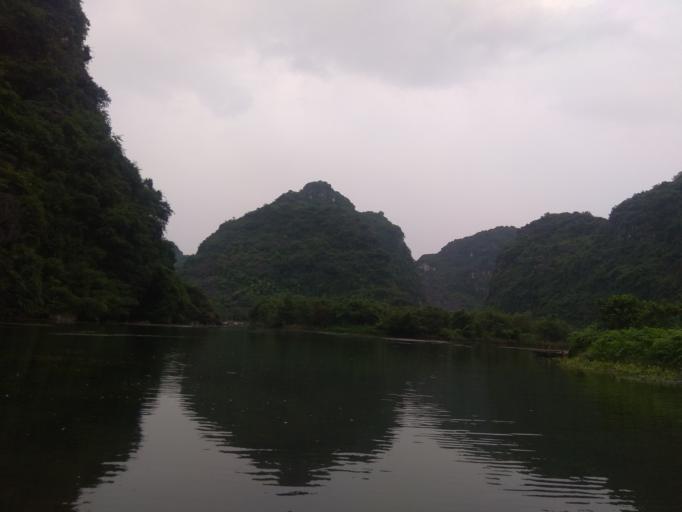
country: VN
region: Ninh Binh
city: Thi Tran Thien Ton
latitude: 20.2655
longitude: 105.9024
